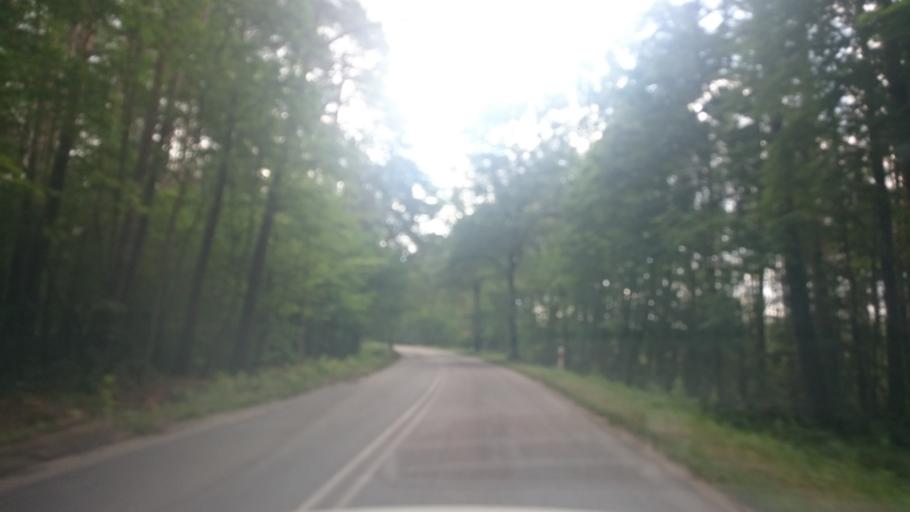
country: PL
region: Pomeranian Voivodeship
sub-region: Powiat koscierski
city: Stara Kiszewa
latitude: 53.9738
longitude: 18.2348
